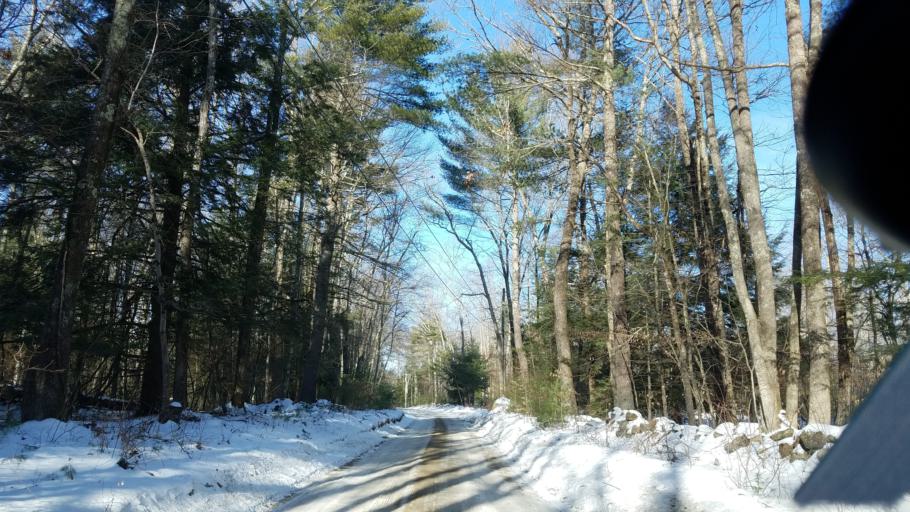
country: US
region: Massachusetts
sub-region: Hampden County
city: Holland
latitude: 41.9650
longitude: -72.0974
